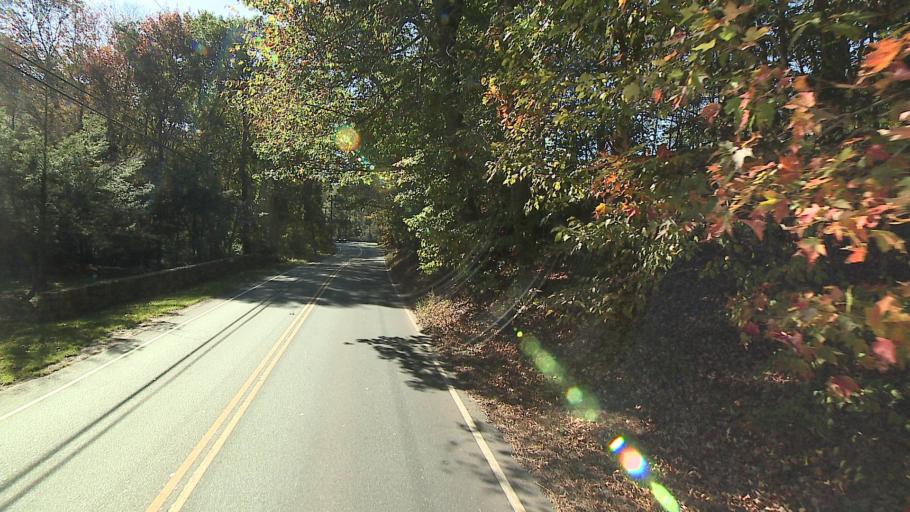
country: US
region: Connecticut
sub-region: Fairfield County
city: Westport
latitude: 41.1867
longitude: -73.3408
